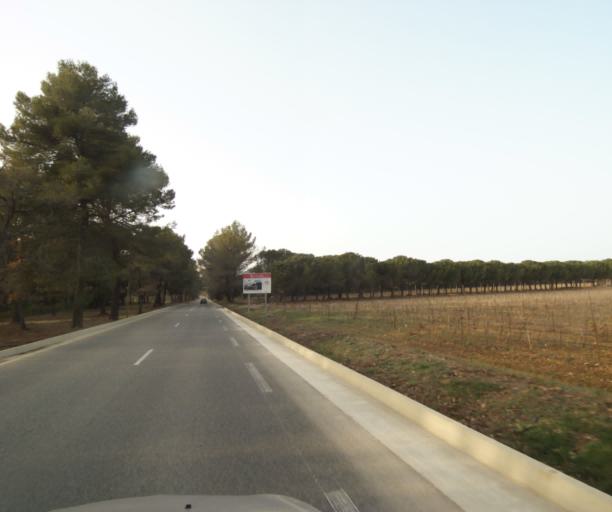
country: FR
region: Provence-Alpes-Cote d'Azur
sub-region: Departement des Bouches-du-Rhone
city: Eguilles
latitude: 43.6135
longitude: 5.3626
